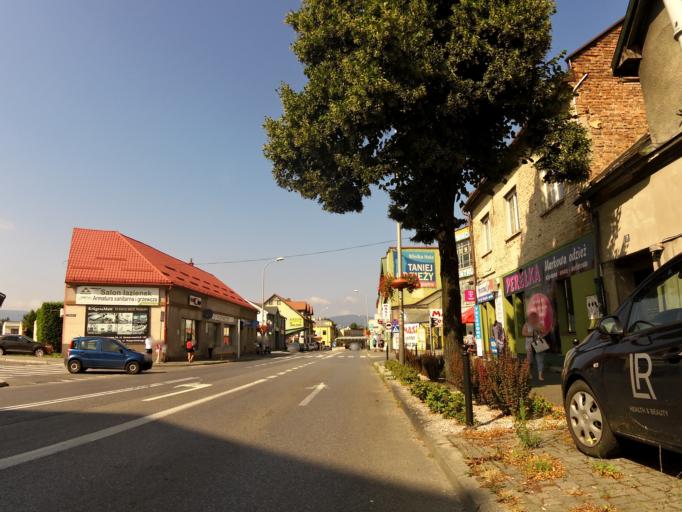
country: PL
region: Silesian Voivodeship
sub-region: Powiat zywiecki
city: Zywiec
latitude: 49.6818
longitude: 19.1889
